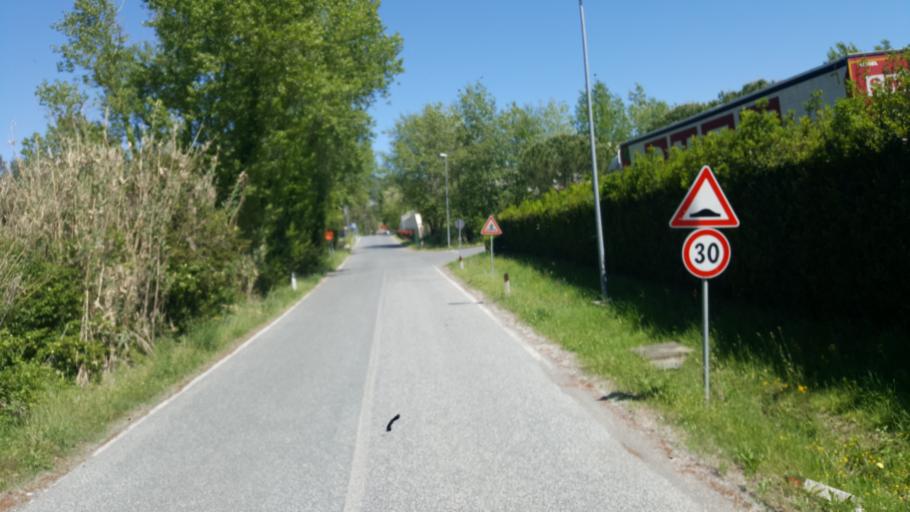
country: IT
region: Tuscany
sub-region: Province of Pisa
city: Castellina Marittima
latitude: 43.4217
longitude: 10.5427
